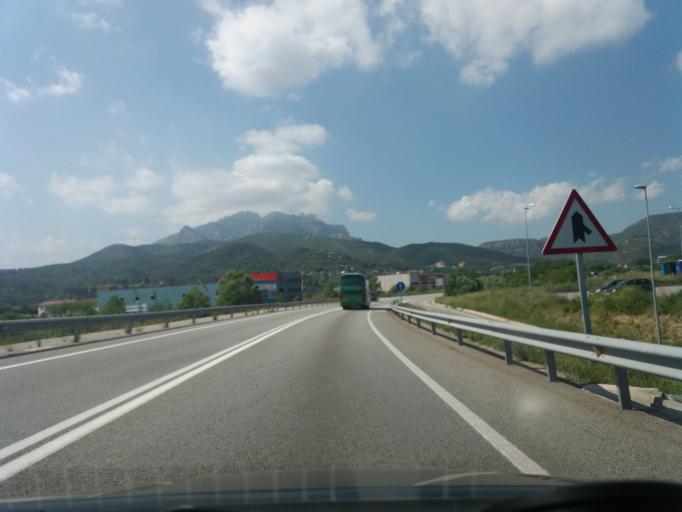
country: ES
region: Catalonia
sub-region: Provincia de Barcelona
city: Olesa de Montserrat
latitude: 41.5449
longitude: 1.8818
